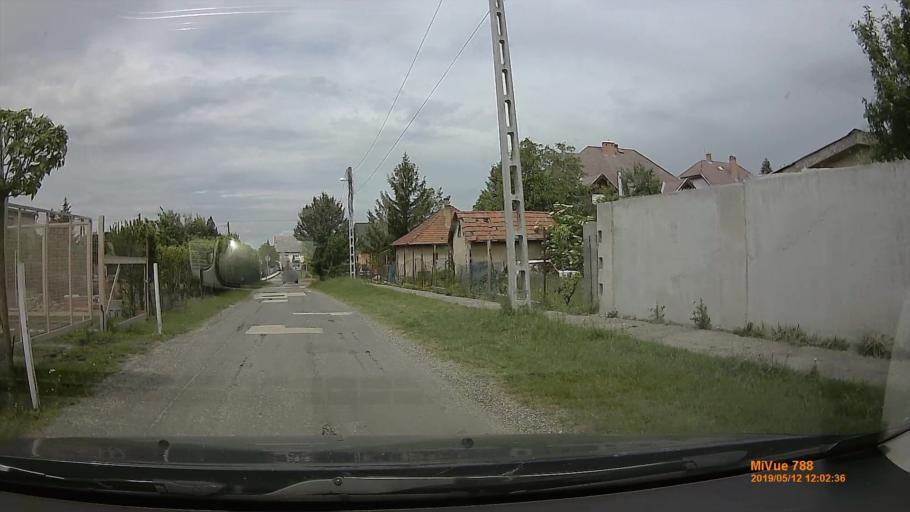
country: HU
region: Budapest
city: Budapest XVII. keruelet
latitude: 47.4706
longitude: 19.2601
